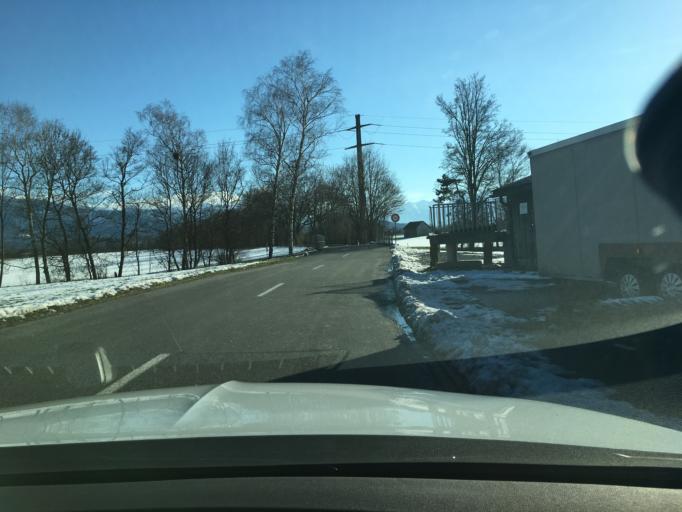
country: CH
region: Saint Gallen
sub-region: Wahlkreis Rheintal
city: Rebstein
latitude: 47.3861
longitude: 9.5796
